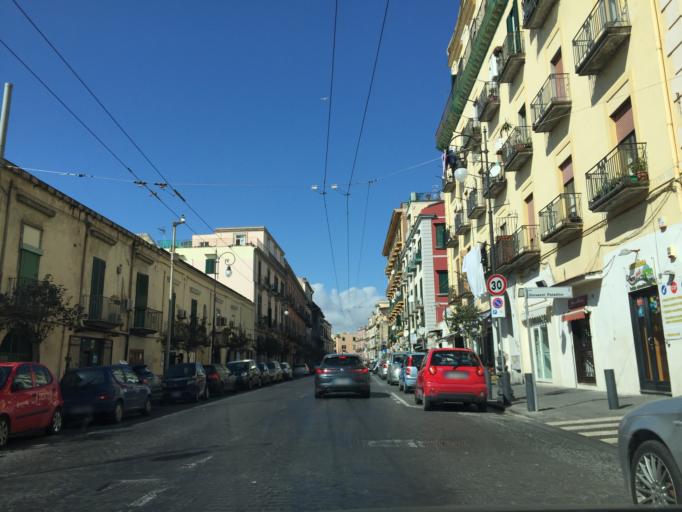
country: IT
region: Campania
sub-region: Provincia di Napoli
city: Portici
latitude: 40.8191
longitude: 14.3290
